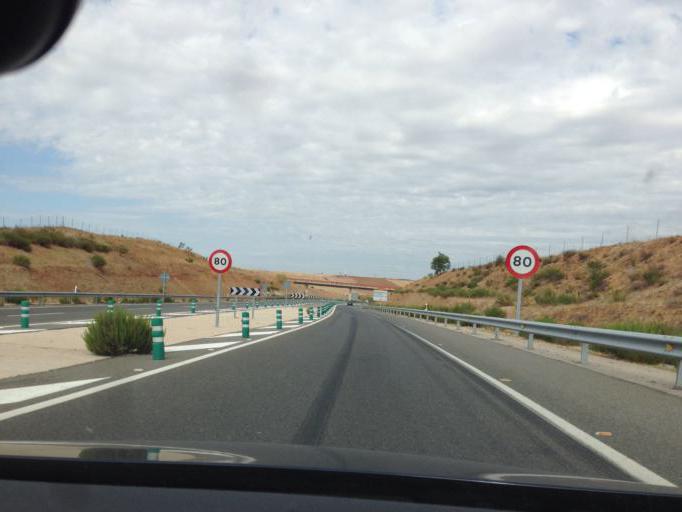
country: ES
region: Madrid
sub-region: Provincia de Madrid
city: Daganzo de Arriba
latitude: 40.5248
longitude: -3.4172
